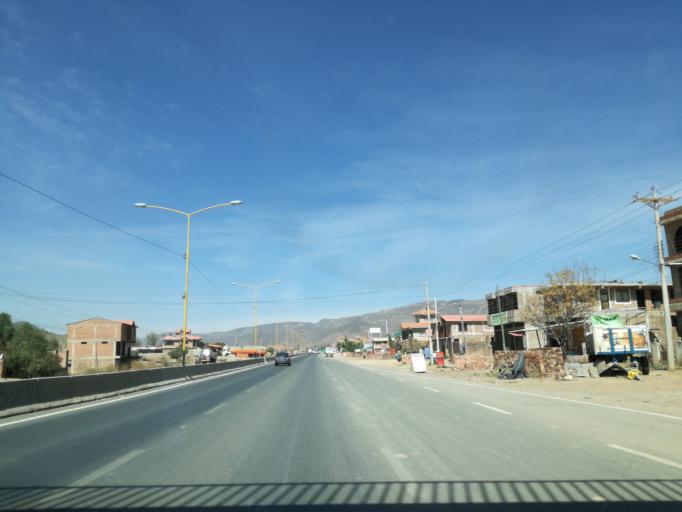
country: BO
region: Cochabamba
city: Sipe Sipe
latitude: -17.4387
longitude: -66.3359
